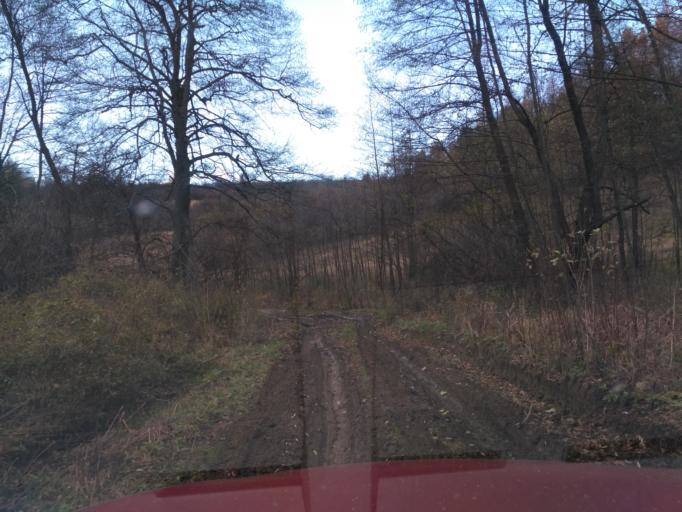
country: SK
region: Presovsky
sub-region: Okres Presov
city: Presov
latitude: 48.9297
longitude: 21.2078
